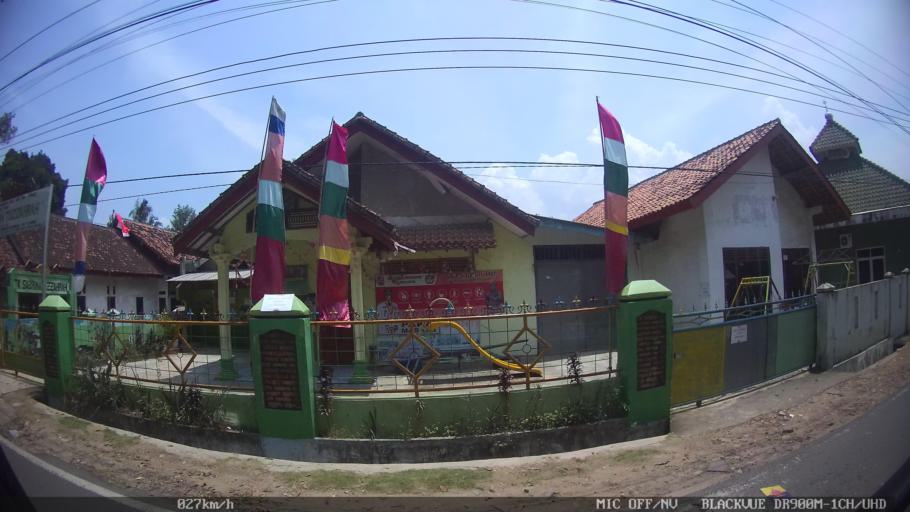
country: ID
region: Lampung
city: Bandarlampung
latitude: -5.4416
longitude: 105.2426
